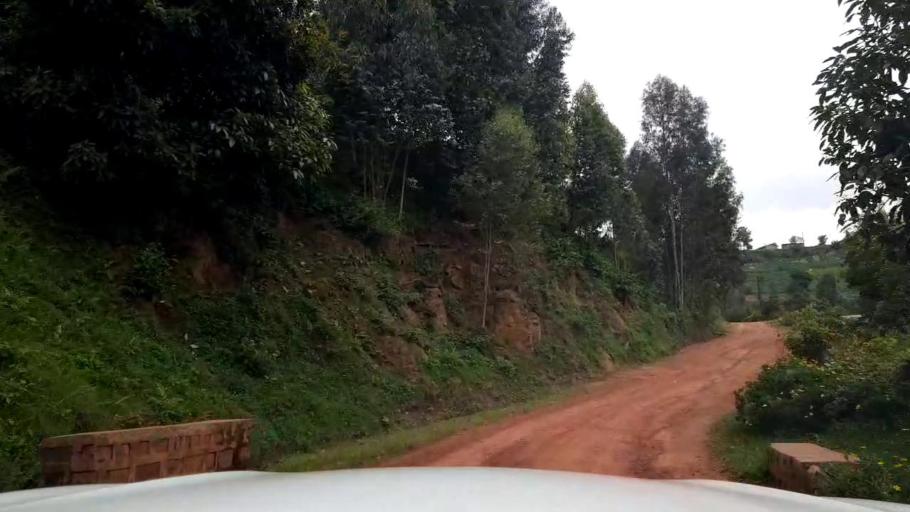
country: RW
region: Northern Province
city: Byumba
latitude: -1.4865
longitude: 29.9276
